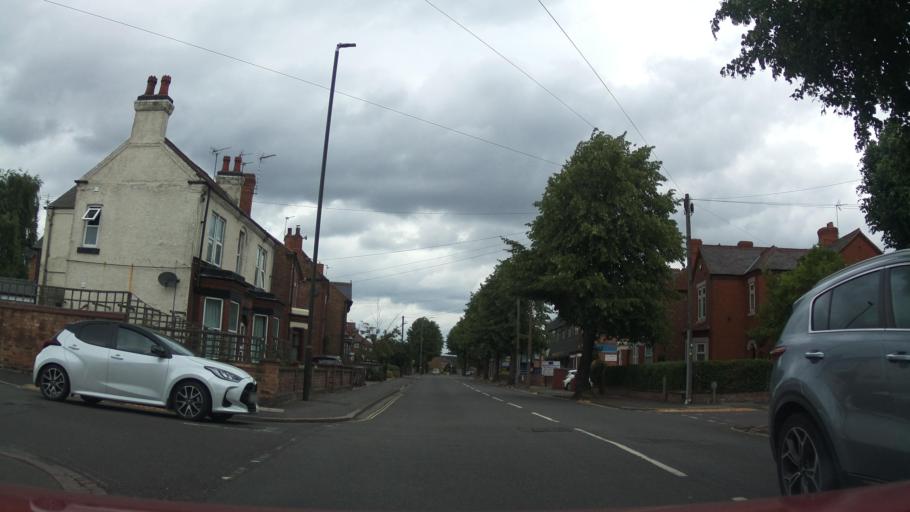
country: GB
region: England
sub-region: Derbyshire
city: Long Eaton
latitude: 52.8876
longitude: -1.2878
